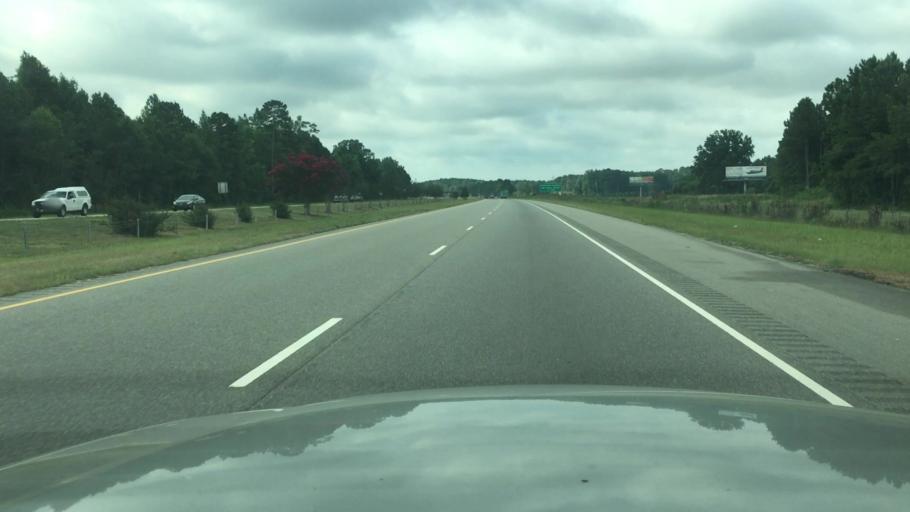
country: US
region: North Carolina
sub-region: Cumberland County
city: Fayetteville
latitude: 35.0197
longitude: -78.8717
